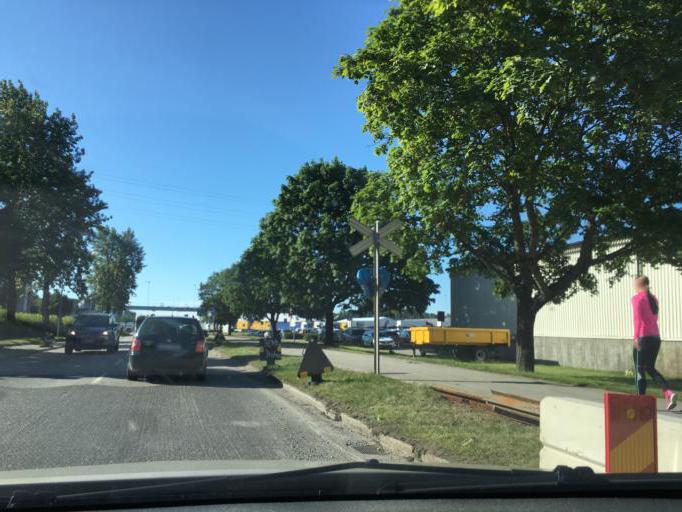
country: SE
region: Stockholm
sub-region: Sodertalje Kommun
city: Pershagen
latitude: 59.1739
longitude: 17.6439
